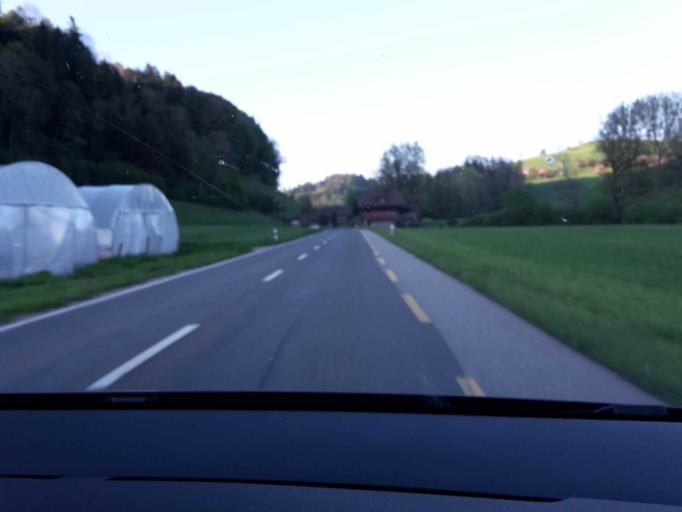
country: CH
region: Bern
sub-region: Emmental District
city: Lutzelfluh
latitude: 47.0274
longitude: 7.6794
